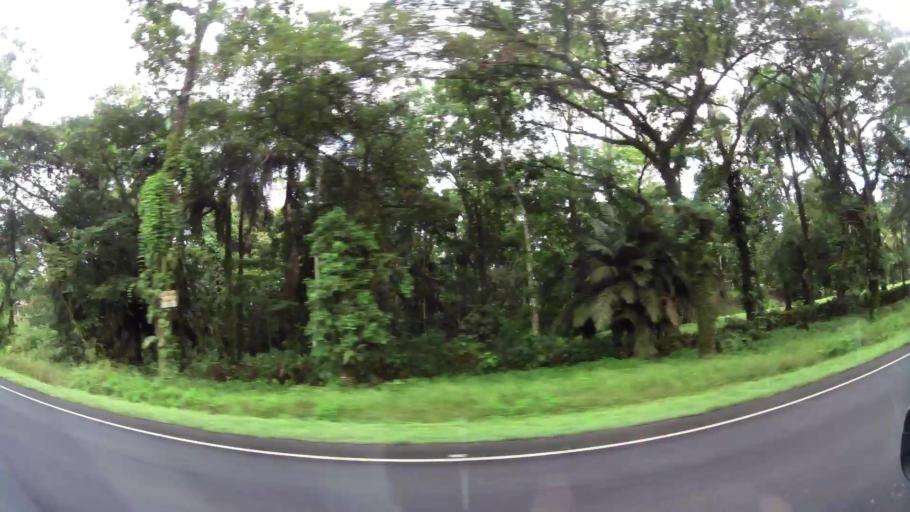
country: CR
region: Limon
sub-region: Canton de Guacimo
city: Guacimo
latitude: 10.2078
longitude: -83.7042
